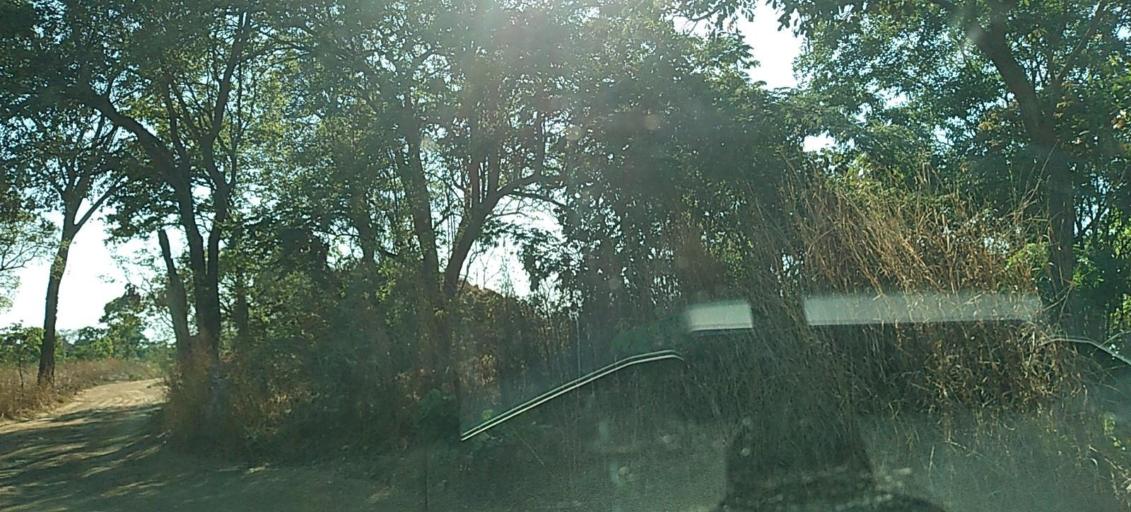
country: ZM
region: Copperbelt
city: Chililabombwe
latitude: -12.3694
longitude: 27.9064
